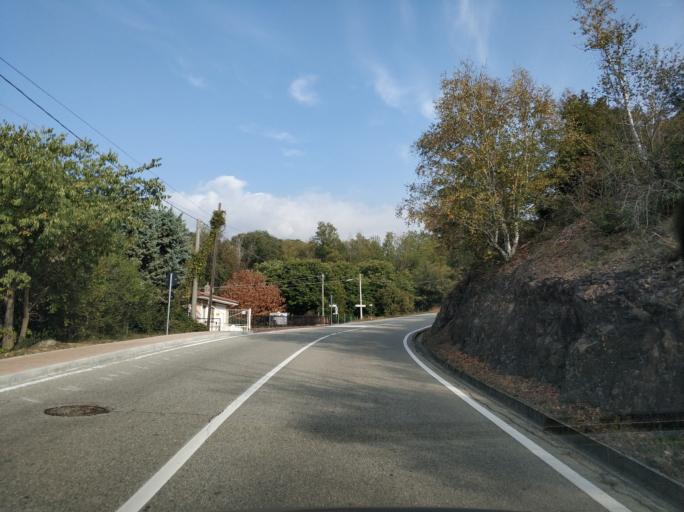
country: IT
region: Piedmont
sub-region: Provincia di Torino
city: Chiaverano
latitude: 45.4887
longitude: 7.8875
